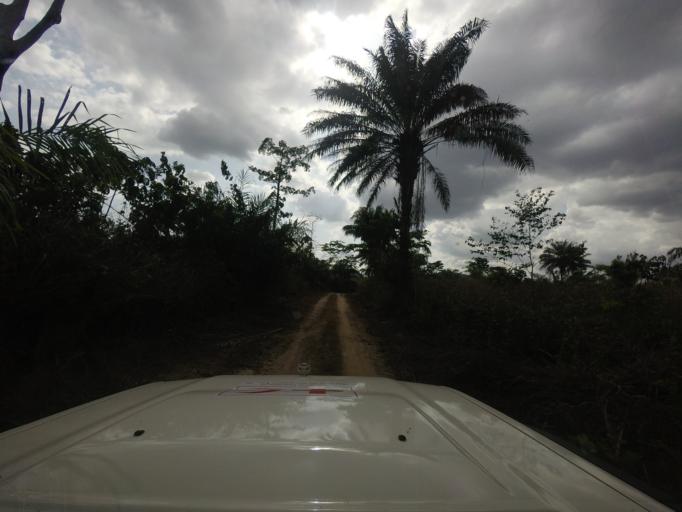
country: LR
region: Lofa
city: Voinjama
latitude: 8.3919
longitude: -9.6127
